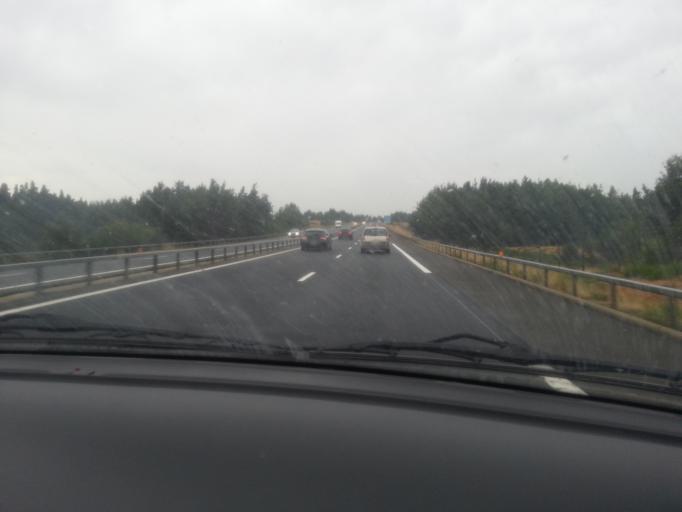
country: FR
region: Languedoc-Roussillon
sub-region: Departement de la Lozere
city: Aumont-Aubrac
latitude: 44.7057
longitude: 3.2777
